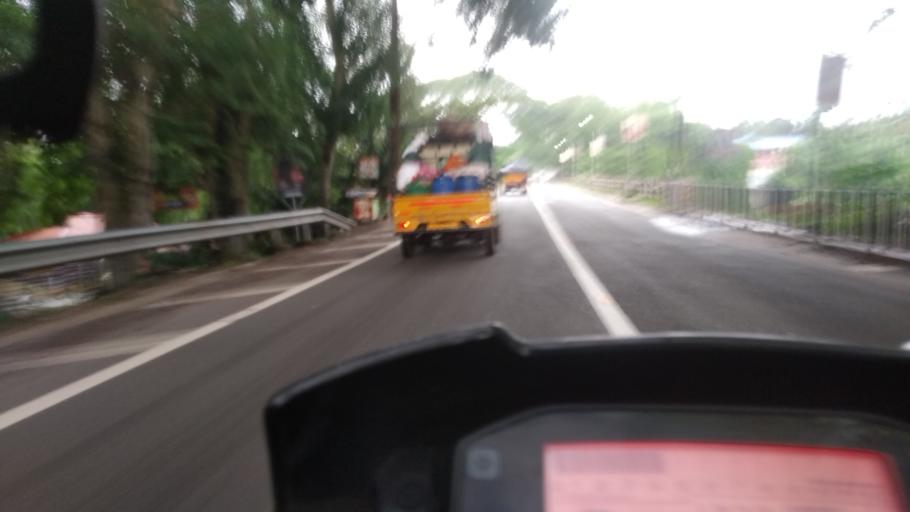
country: IN
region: Kerala
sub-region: Thiruvananthapuram
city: Attingal
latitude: 8.7092
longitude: 76.8135
